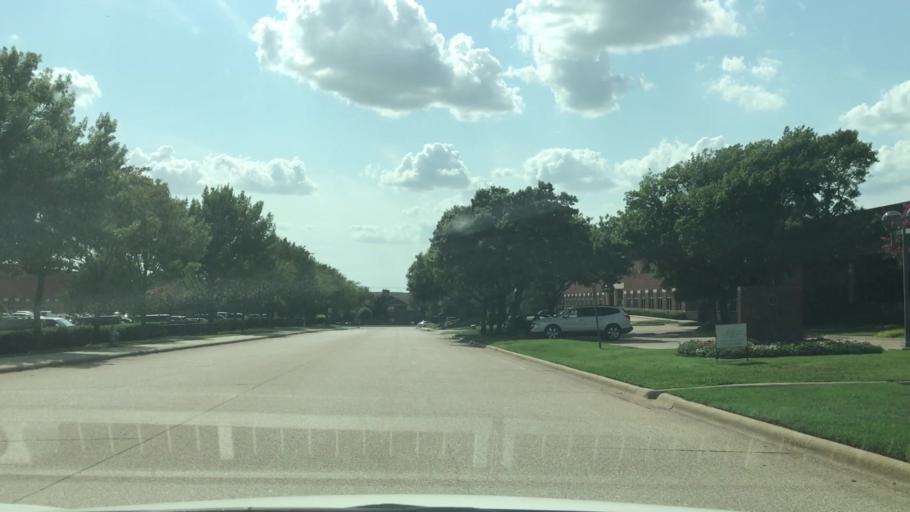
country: US
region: Texas
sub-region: Dallas County
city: Addison
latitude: 32.9739
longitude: -96.8492
